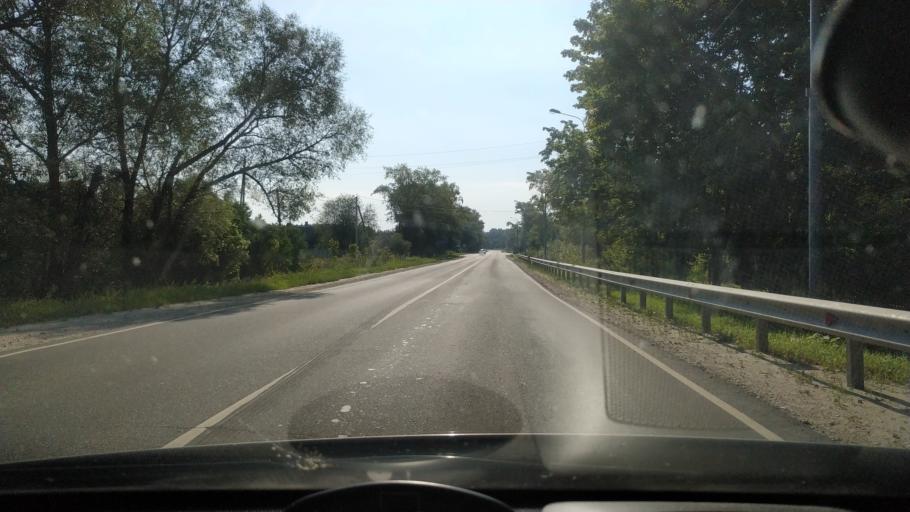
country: RU
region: Moskovskaya
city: Dmitrovskiy Pogost
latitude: 55.2348
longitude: 39.9057
